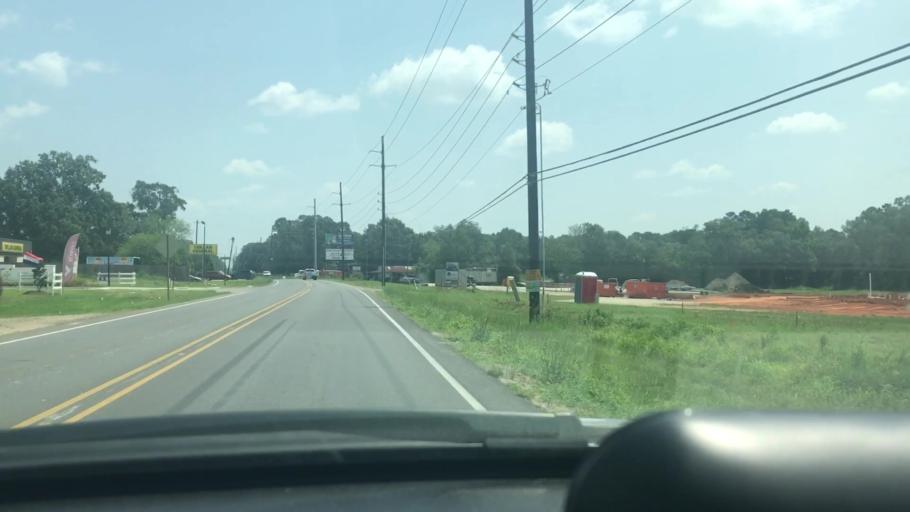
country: US
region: Louisiana
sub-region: Livingston Parish
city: Denham Springs
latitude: 30.4829
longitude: -90.9134
